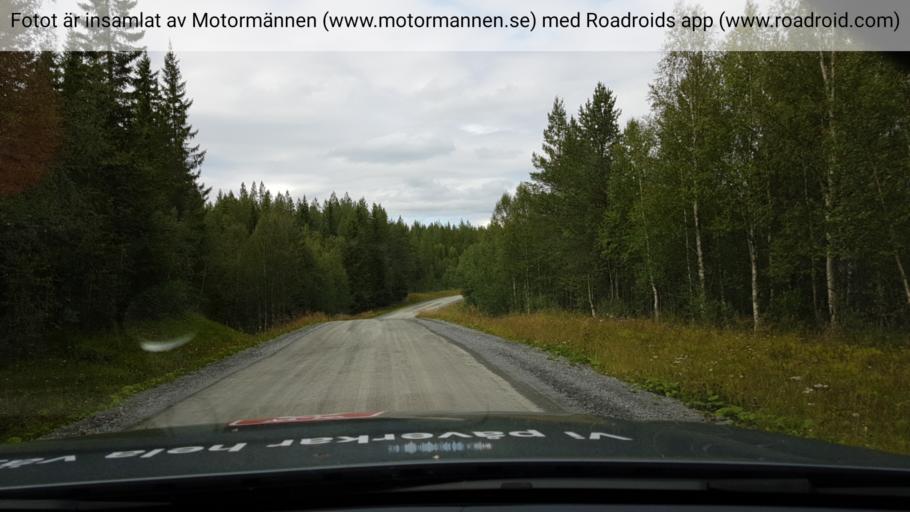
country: SE
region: Jaemtland
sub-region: Krokoms Kommun
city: Valla
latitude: 63.6713
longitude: 13.6995
